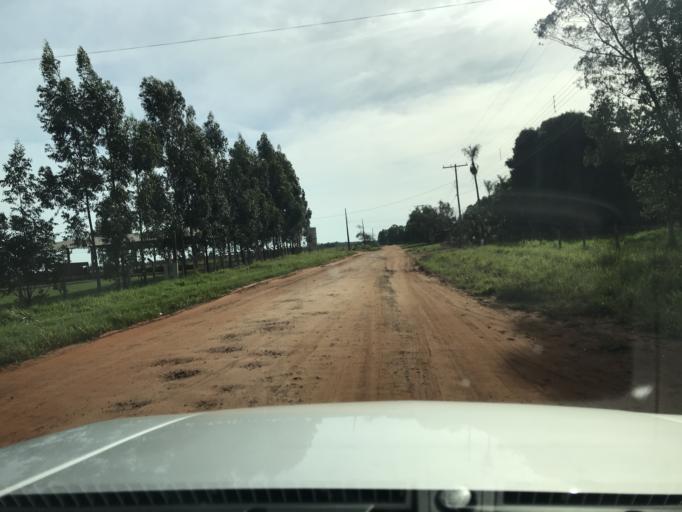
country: BR
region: Mato Grosso do Sul
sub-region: Iguatemi
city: Iguatemi
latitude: -23.6608
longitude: -54.5684
